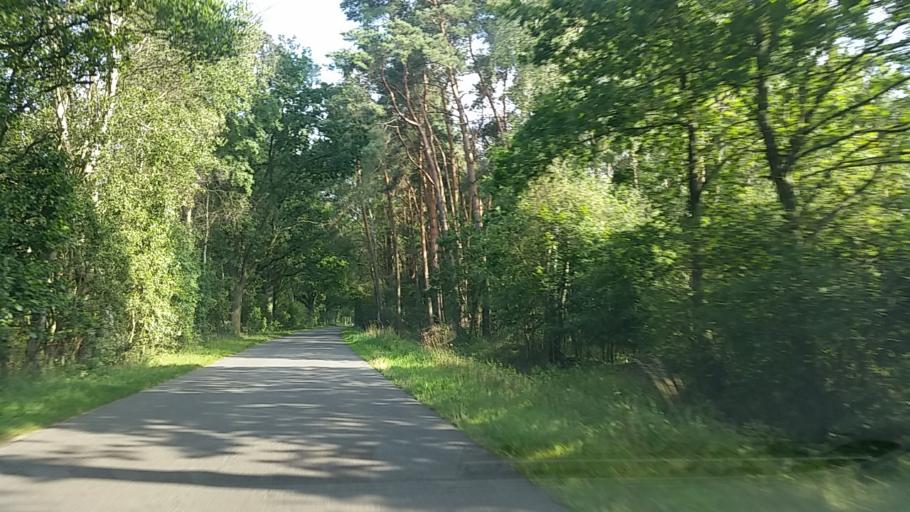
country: DE
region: Lower Saxony
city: Radbruch
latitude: 53.3221
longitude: 10.2440
